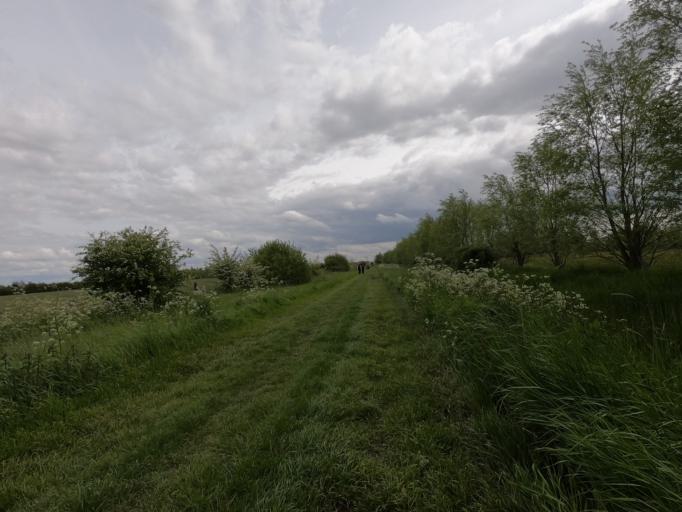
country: BE
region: Flanders
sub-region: Provincie West-Vlaanderen
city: Alveringem
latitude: 50.9462
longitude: 2.7508
